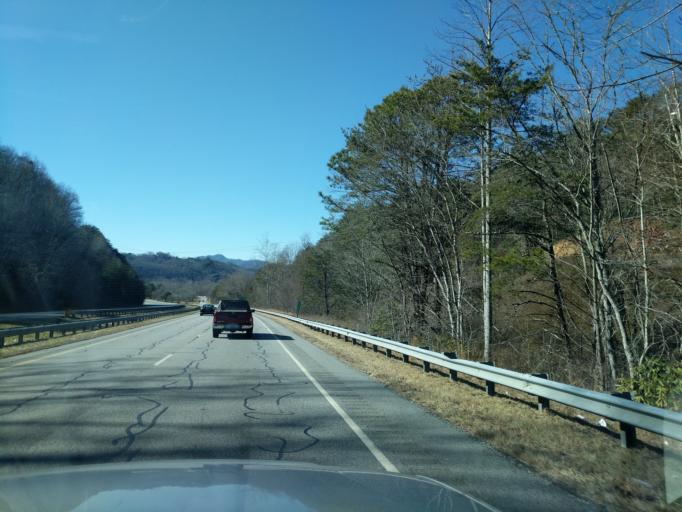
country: US
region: North Carolina
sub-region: Swain County
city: Bryson City
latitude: 35.4355
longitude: -83.3888
